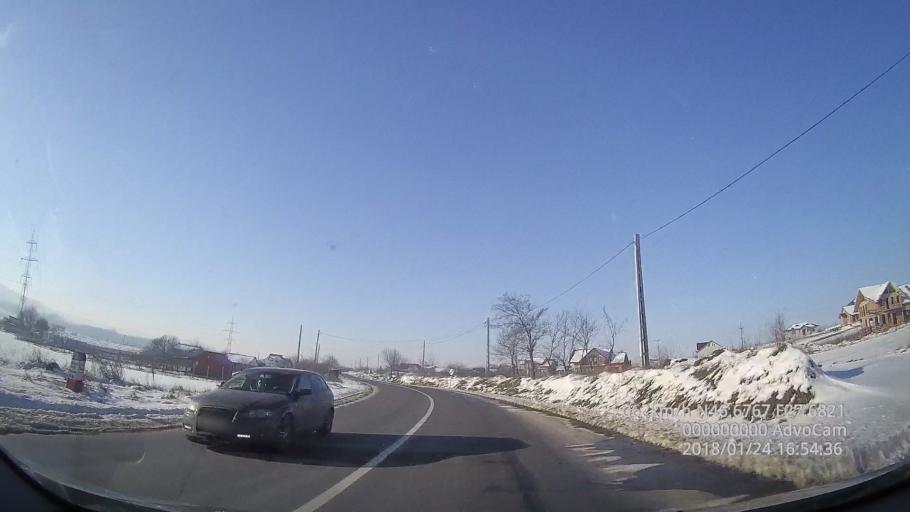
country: RO
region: Vaslui
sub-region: Municipiul Vaslui
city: Brodoc
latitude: 46.6770
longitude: 27.6816
